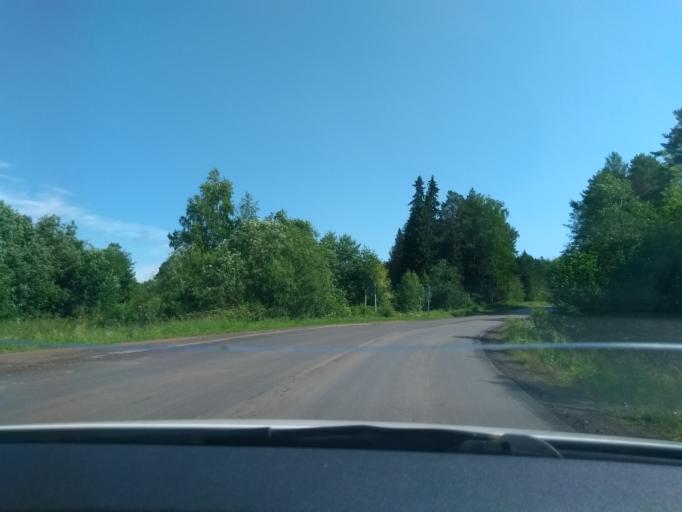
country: RU
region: Perm
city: Bershet'
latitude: 57.8207
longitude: 56.5061
